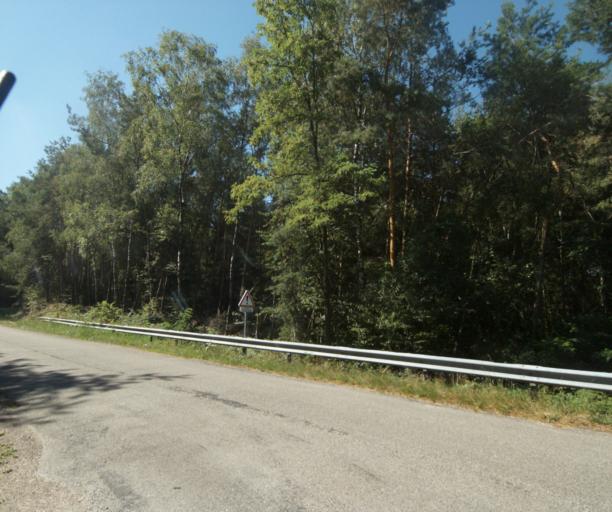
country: FR
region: Lorraine
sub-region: Departement des Vosges
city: Epinal
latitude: 48.1688
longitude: 6.4844
